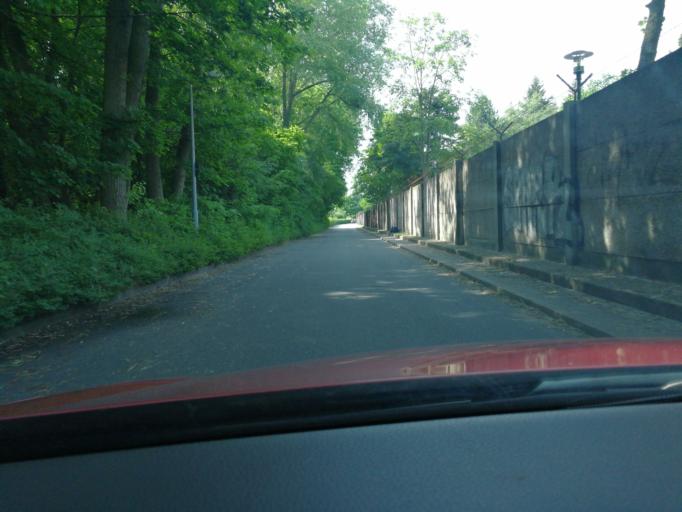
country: DE
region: Berlin
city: Reinickendorf
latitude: 52.5525
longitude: 13.3239
